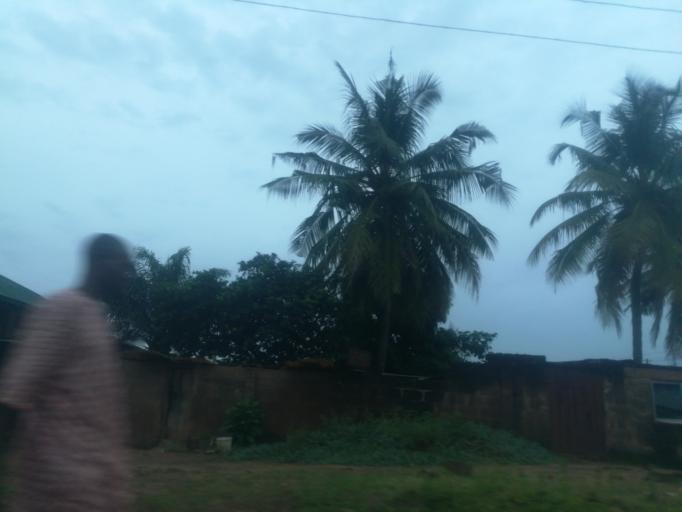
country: NG
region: Oyo
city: Ibadan
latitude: 7.4022
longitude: 3.9672
